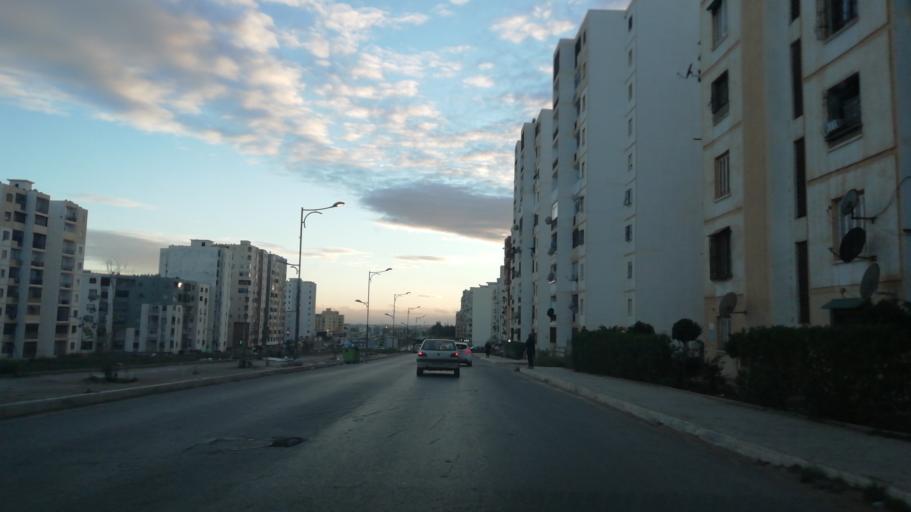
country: DZ
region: Oran
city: Bir el Djir
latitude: 35.7000
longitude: -0.5624
